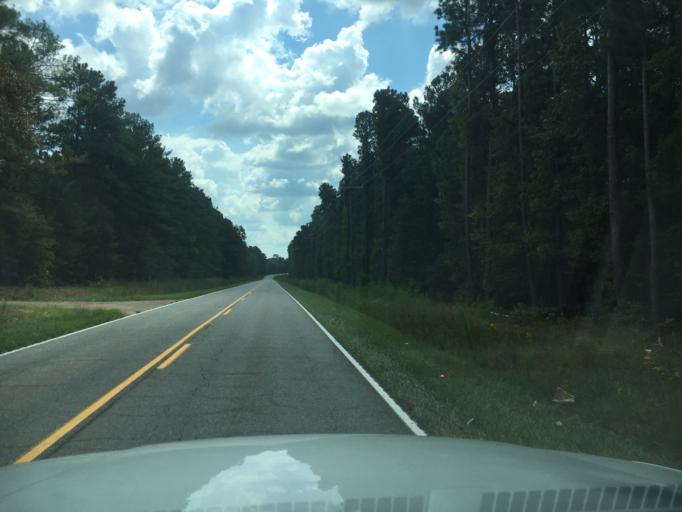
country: US
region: South Carolina
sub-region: Greenwood County
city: Greenwood
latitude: 34.0894
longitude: -82.1312
